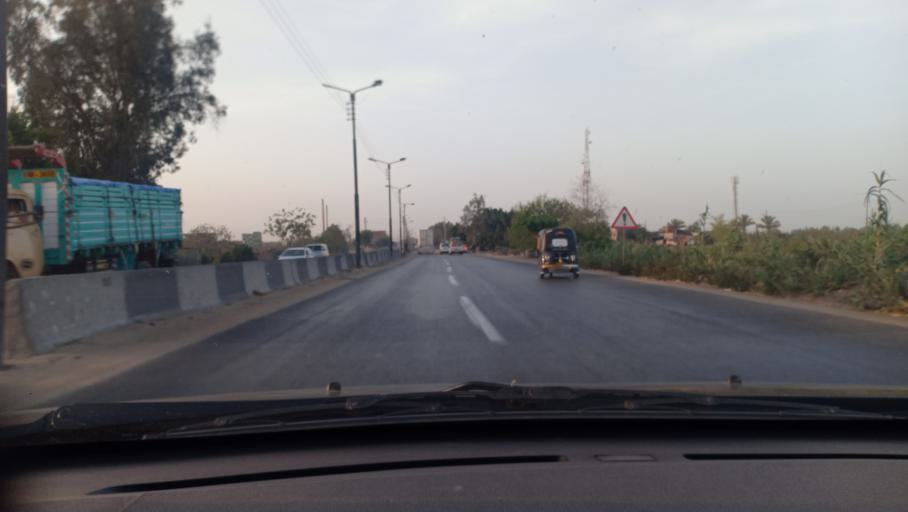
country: EG
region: Muhafazat al Gharbiyah
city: Zifta
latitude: 30.6218
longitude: 31.2784
